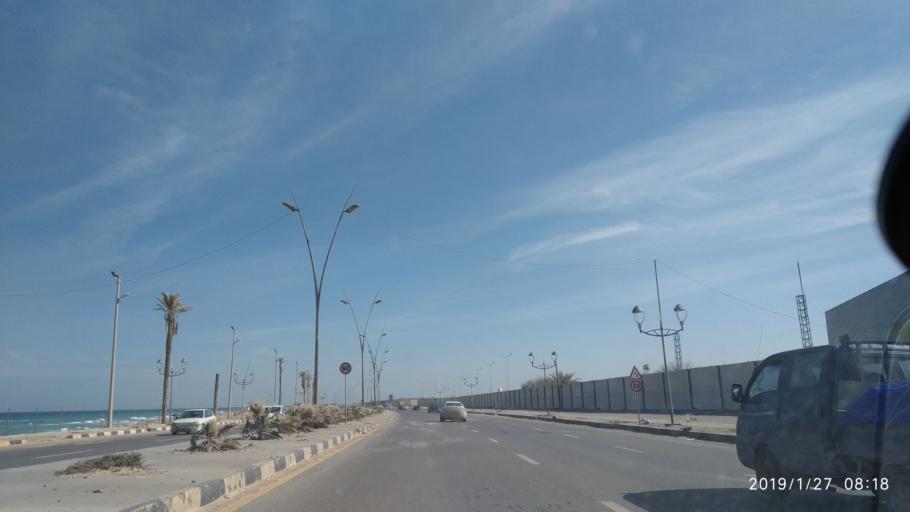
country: LY
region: Tripoli
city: Tagiura
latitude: 32.9084
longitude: 13.2802
